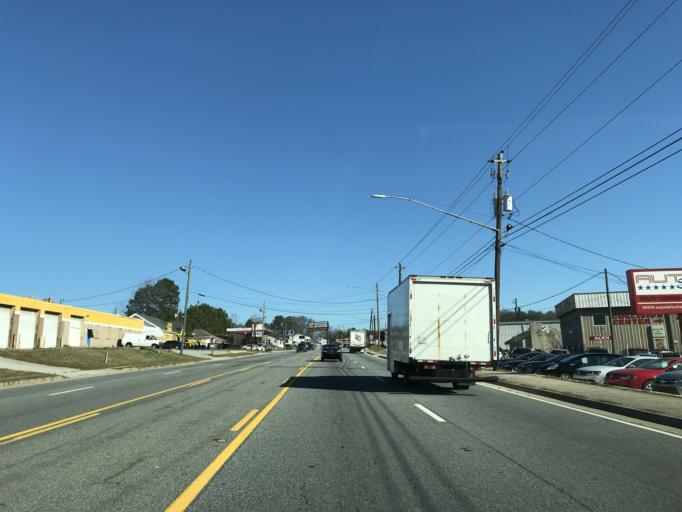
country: US
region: Georgia
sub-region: DeKalb County
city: Tucker
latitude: 33.8481
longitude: -84.2262
